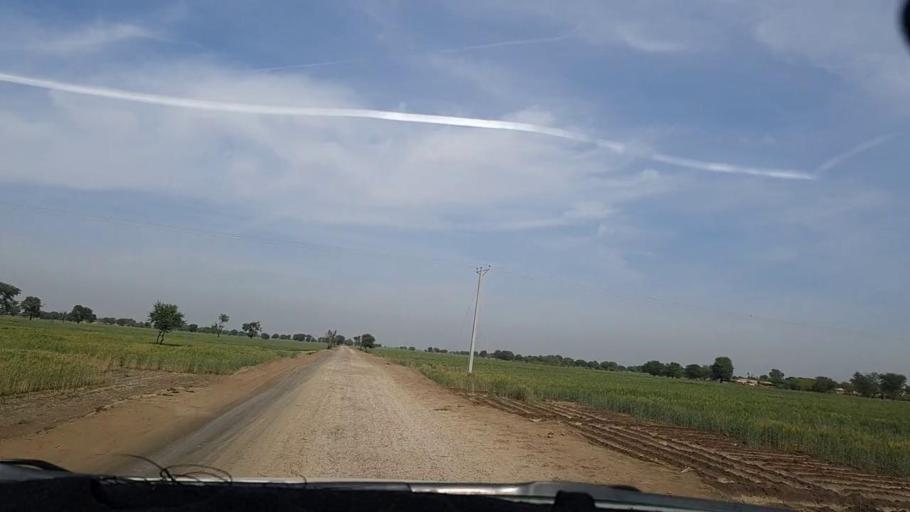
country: PK
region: Sindh
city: Dhoro Naro
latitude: 25.4423
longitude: 69.4970
